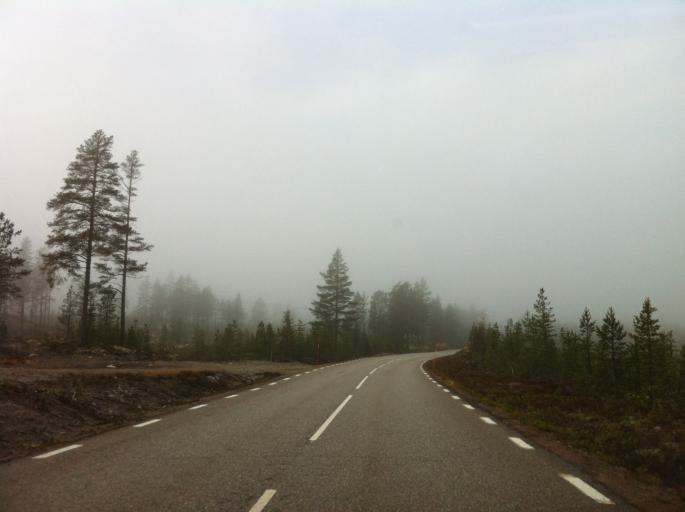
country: NO
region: Hedmark
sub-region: Engerdal
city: Engerdal
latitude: 61.9765
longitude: 12.4948
